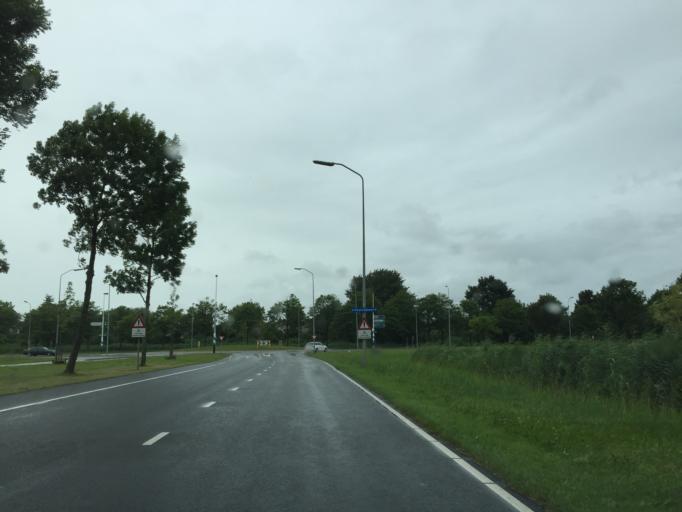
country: NL
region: Flevoland
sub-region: Gemeente Lelystad
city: Lelystad
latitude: 52.5191
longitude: 5.4526
